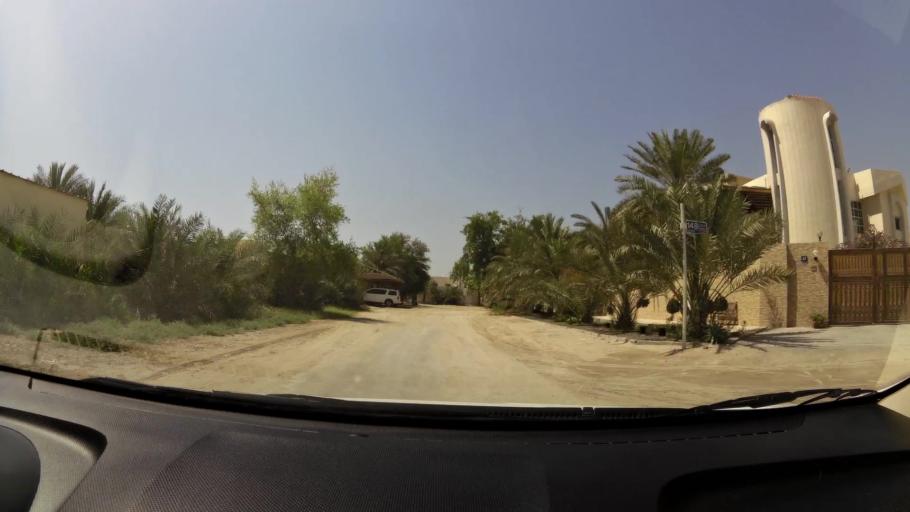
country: AE
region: Ajman
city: Ajman
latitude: 25.4196
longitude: 55.4717
